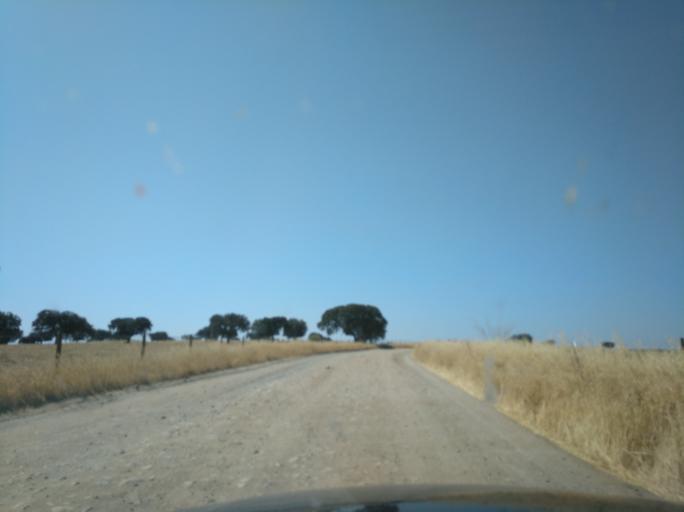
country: PT
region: Portalegre
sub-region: Campo Maior
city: Campo Maior
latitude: 39.0178
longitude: -6.9826
